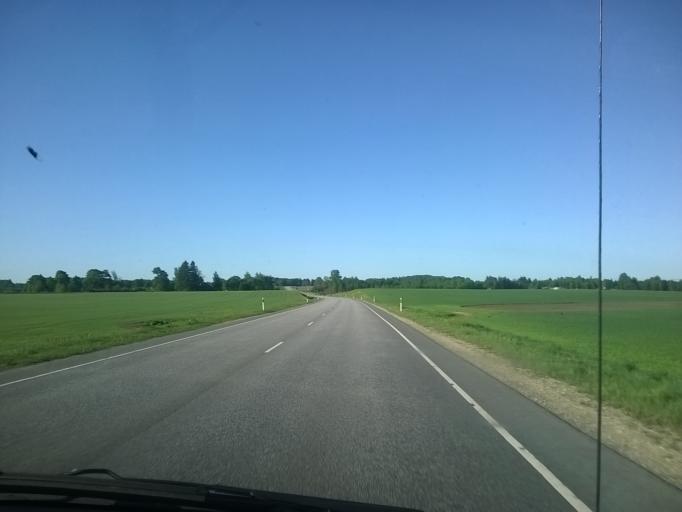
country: EE
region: Tartu
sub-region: Elva linn
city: Elva
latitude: 58.1993
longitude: 26.3541
